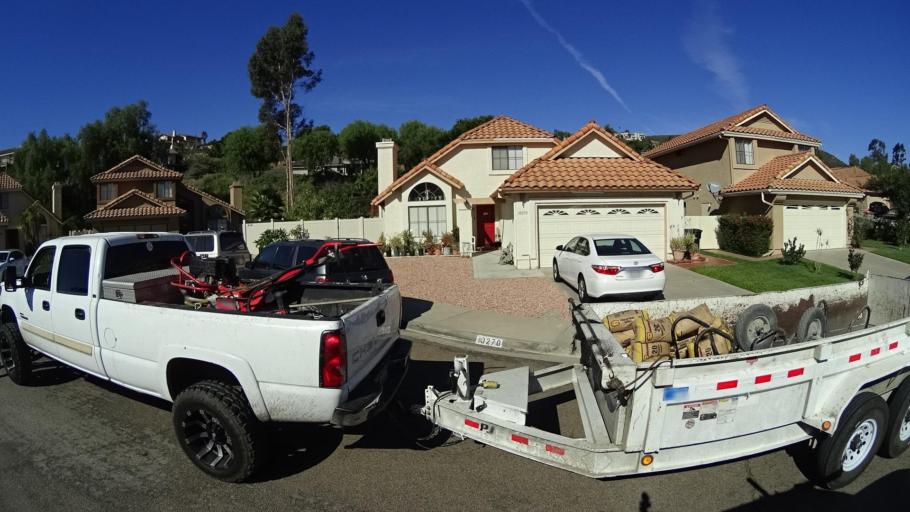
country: US
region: California
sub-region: San Diego County
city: La Presa
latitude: 32.7174
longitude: -116.9790
